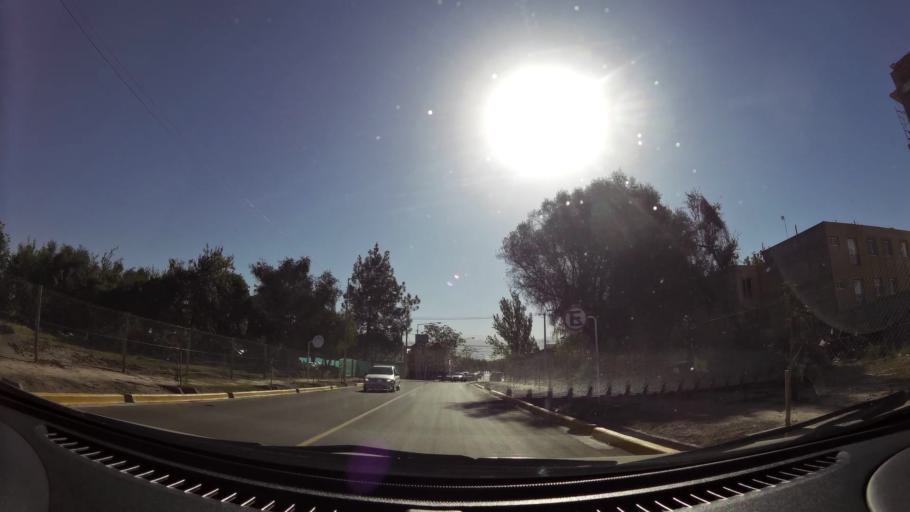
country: AR
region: Mendoza
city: Mendoza
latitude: -32.9052
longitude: -68.8174
